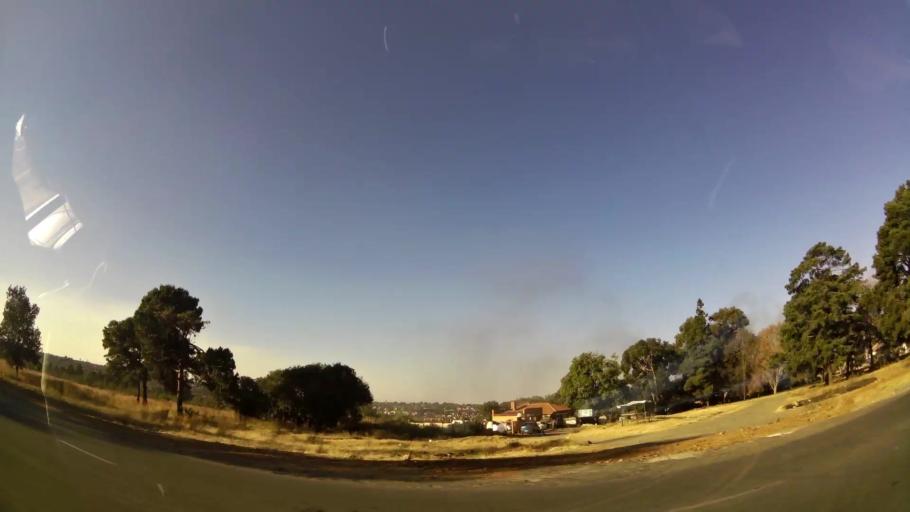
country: ZA
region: Gauteng
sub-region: City of Johannesburg Metropolitan Municipality
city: Roodepoort
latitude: -26.1711
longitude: 27.8737
